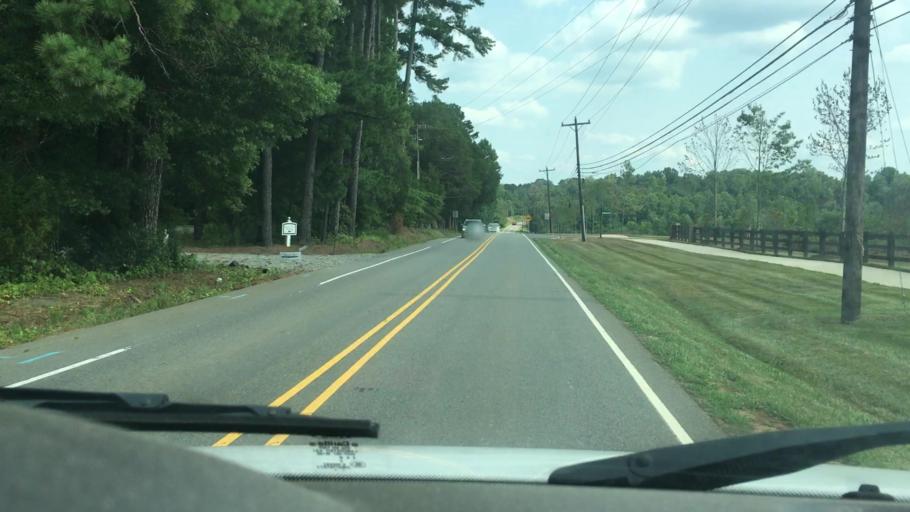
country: US
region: North Carolina
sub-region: Gaston County
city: Davidson
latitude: 35.4764
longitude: -80.8190
